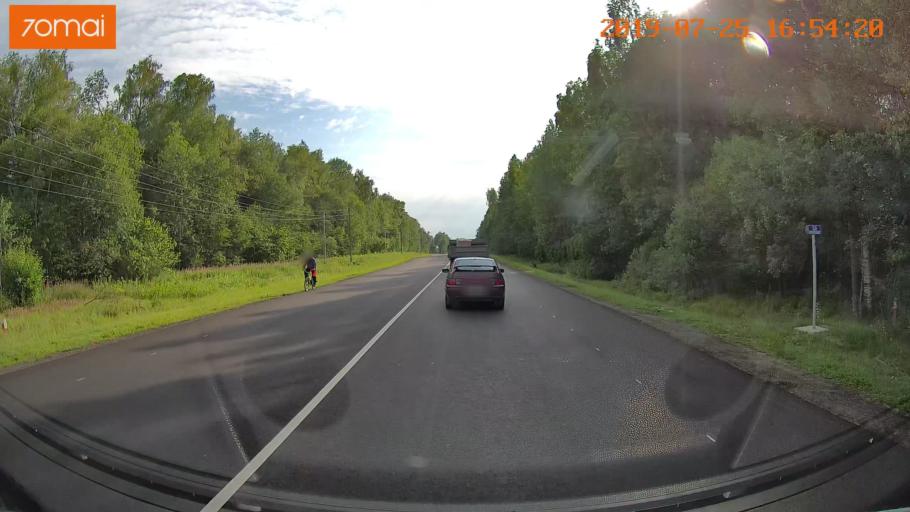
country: RU
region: Ivanovo
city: Furmanov
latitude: 57.2995
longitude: 41.1950
